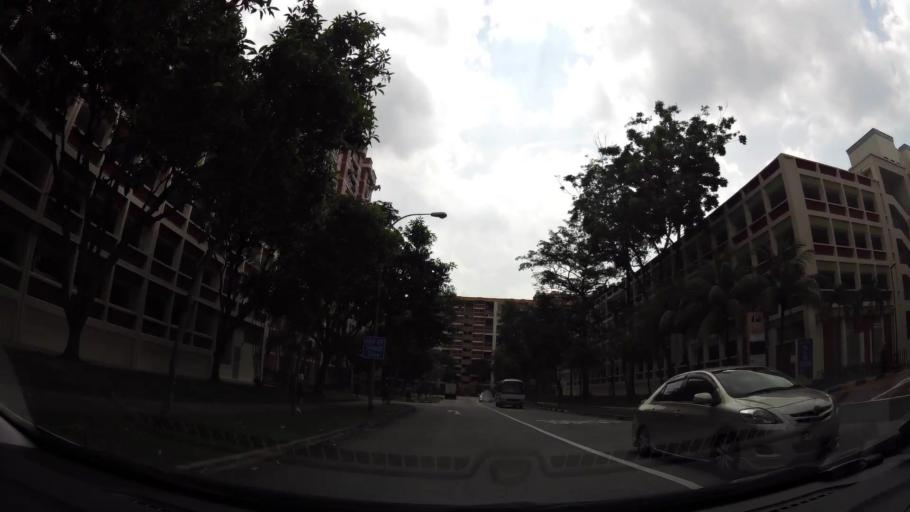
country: SG
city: Singapore
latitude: 1.3568
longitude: 103.9363
